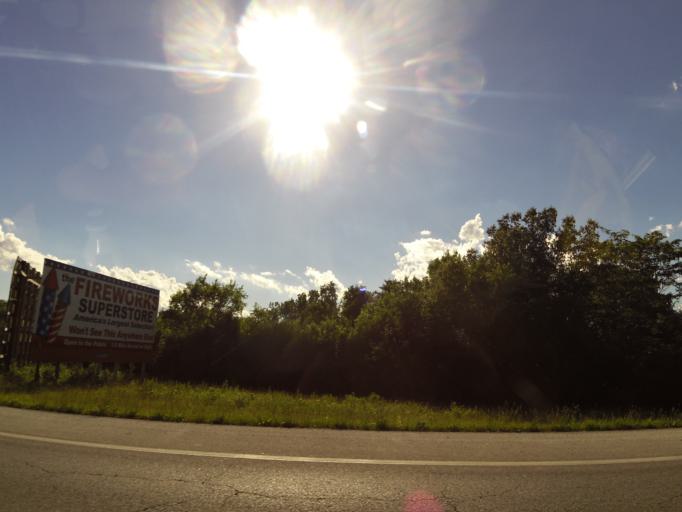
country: US
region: Missouri
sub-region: Marion County
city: Hannibal
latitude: 39.6623
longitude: -91.4183
